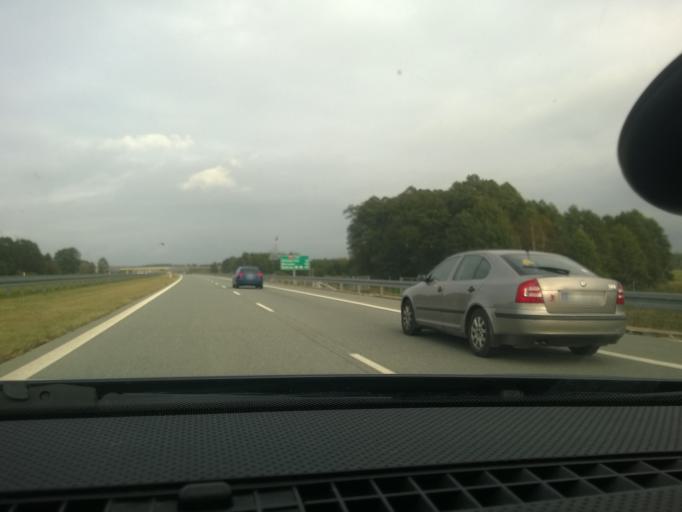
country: PL
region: Lodz Voivodeship
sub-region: Powiat pabianicki
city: Pabianice
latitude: 51.6170
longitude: 19.3749
